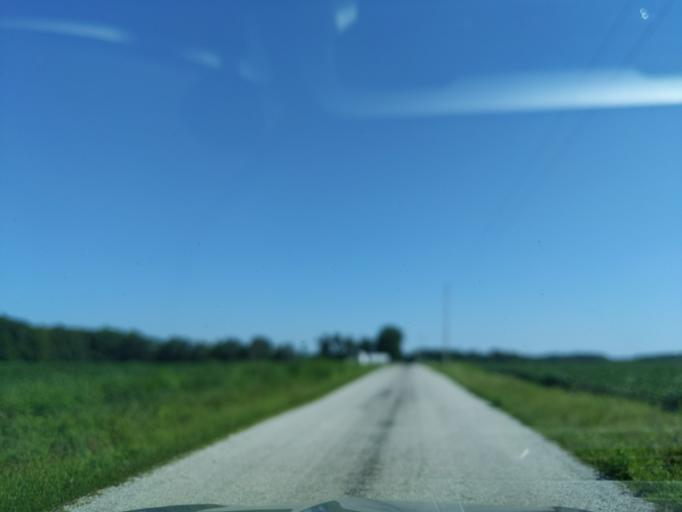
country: US
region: Indiana
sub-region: Ripley County
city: Osgood
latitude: 39.1070
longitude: -85.4323
